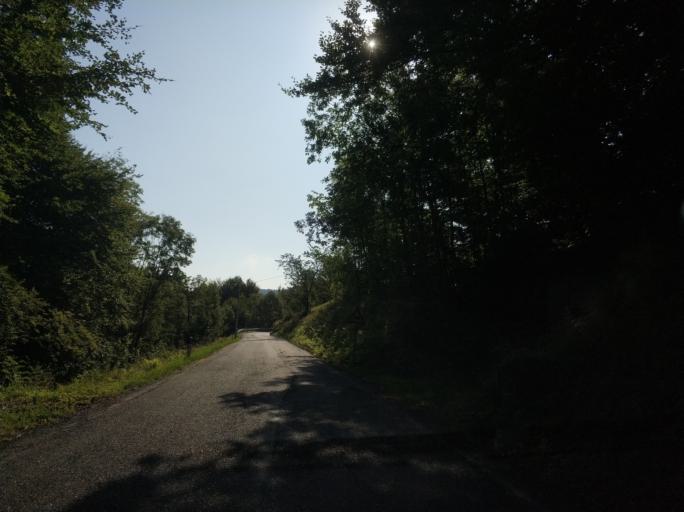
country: IT
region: Piedmont
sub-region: Provincia di Torino
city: Viu
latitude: 45.2083
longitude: 7.3765
